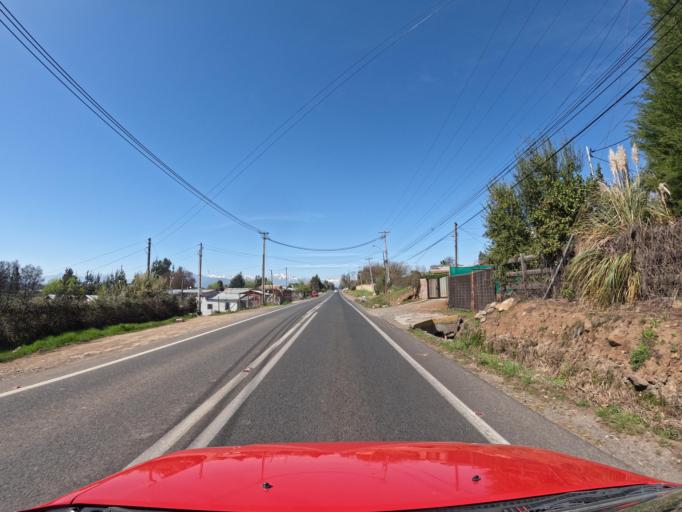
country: CL
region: Maule
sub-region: Provincia de Curico
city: Teno
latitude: -34.9632
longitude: -71.0718
